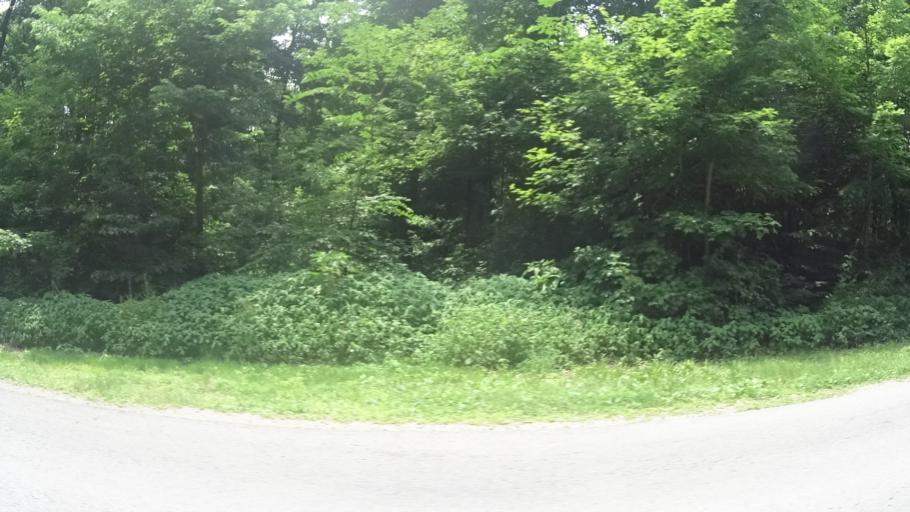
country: US
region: Ohio
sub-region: Erie County
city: Milan
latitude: 41.2903
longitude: -82.6460
